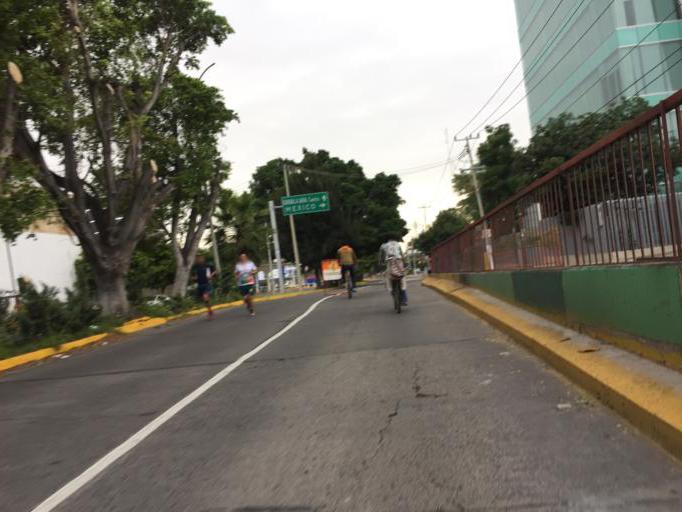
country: MX
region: Jalisco
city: Guadalajara
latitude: 20.6667
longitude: -103.3781
